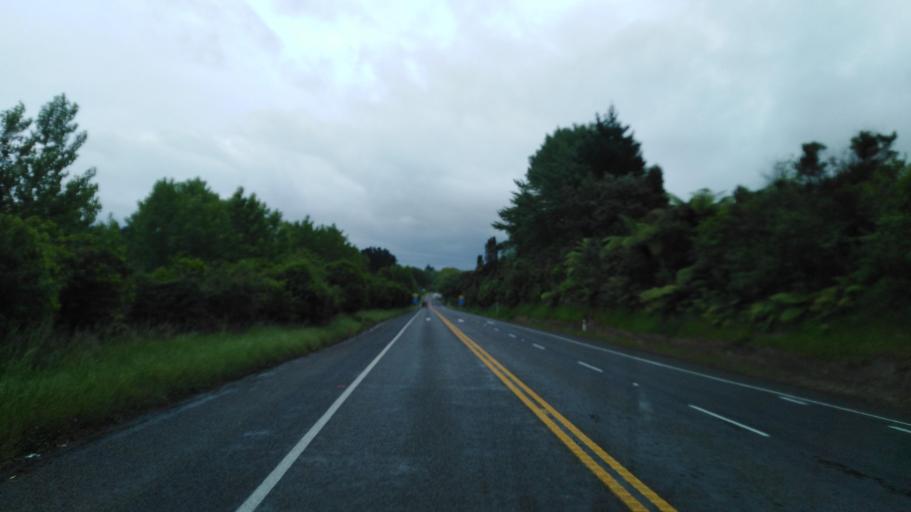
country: NZ
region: Wellington
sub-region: Kapiti Coast District
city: Otaki
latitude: -40.7367
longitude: 175.1868
